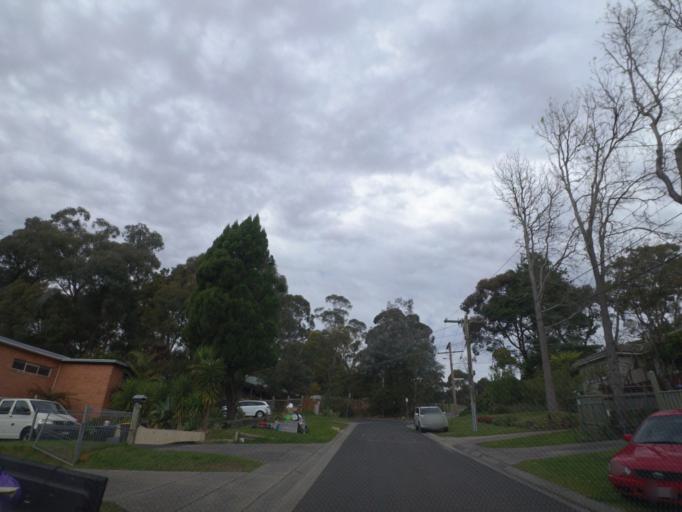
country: AU
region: Victoria
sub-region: Knox
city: The Basin
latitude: -37.8590
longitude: 145.3218
